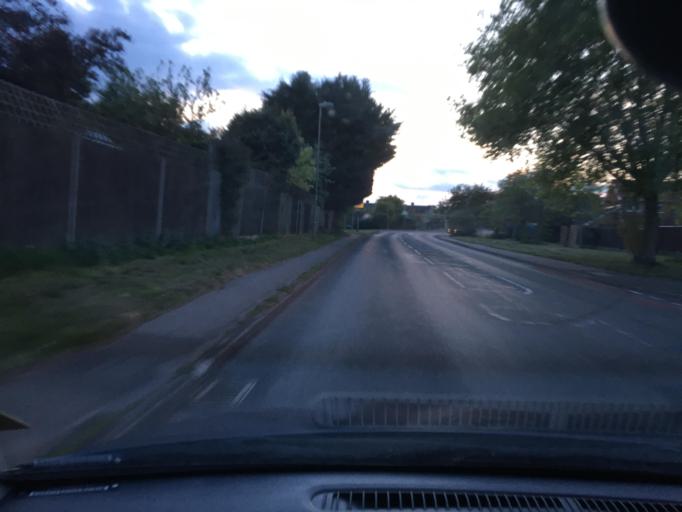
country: GB
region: England
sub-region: Bracknell Forest
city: Sandhurst
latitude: 51.3347
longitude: -0.7864
